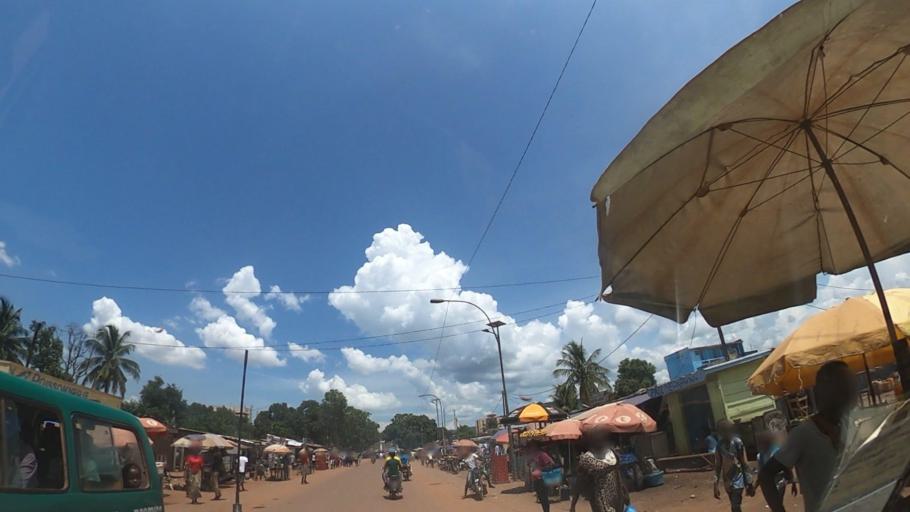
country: CF
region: Bangui
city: Bangui
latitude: 4.3636
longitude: 18.5612
